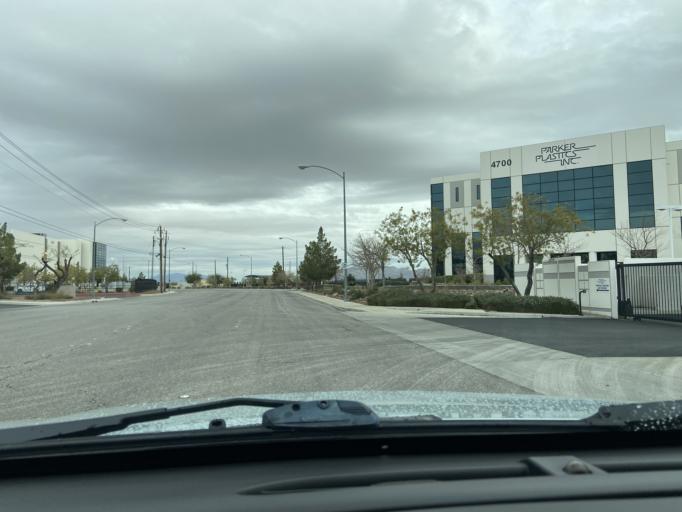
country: US
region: Nevada
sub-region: Clark County
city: Nellis Air Force Base
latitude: 36.2470
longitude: -115.1028
